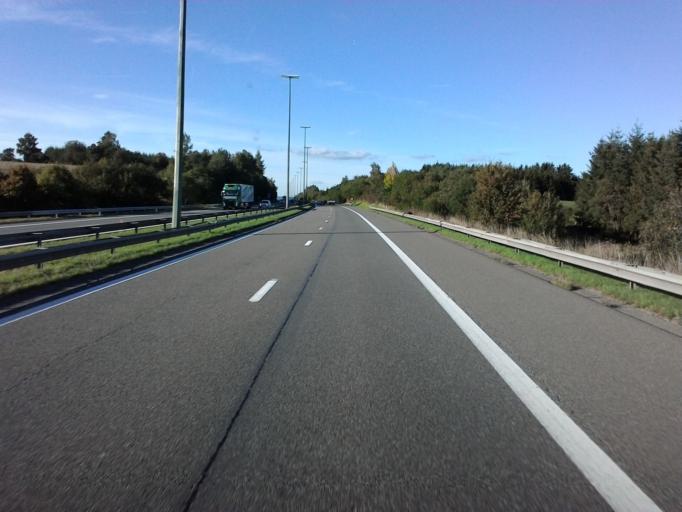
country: BE
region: Wallonia
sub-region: Province du Luxembourg
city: Houffalize
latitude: 50.1025
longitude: 5.7595
